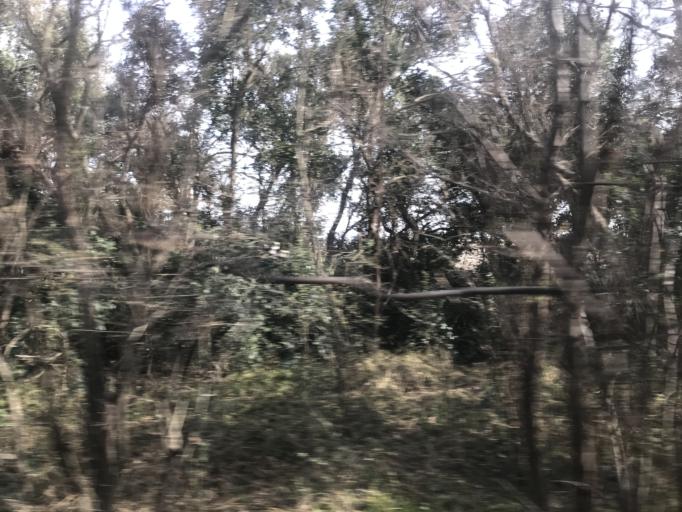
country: AR
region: Cordoba
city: Laguna Larga
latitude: -31.7639
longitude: -63.8142
